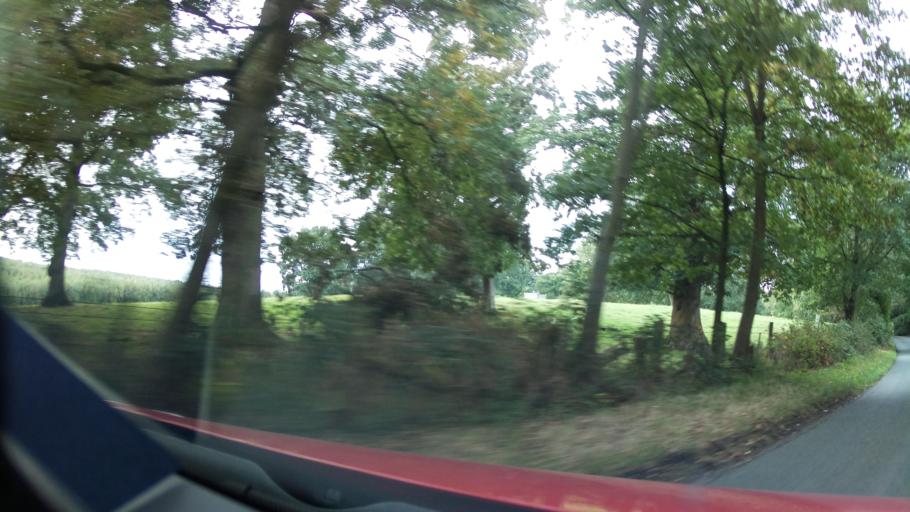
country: GB
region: England
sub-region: Staffordshire
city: Barlaston
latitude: 52.9300
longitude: -2.1989
